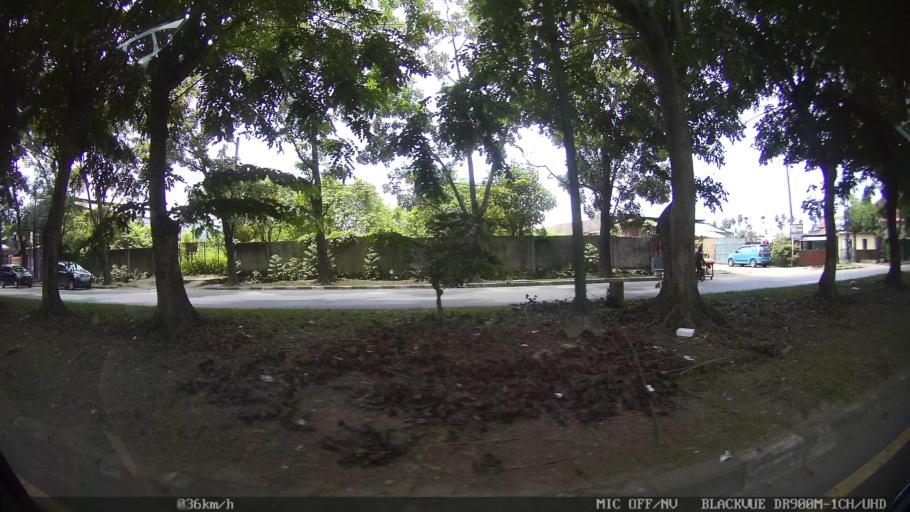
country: ID
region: North Sumatra
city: Sunggal
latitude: 3.5408
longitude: 98.6343
